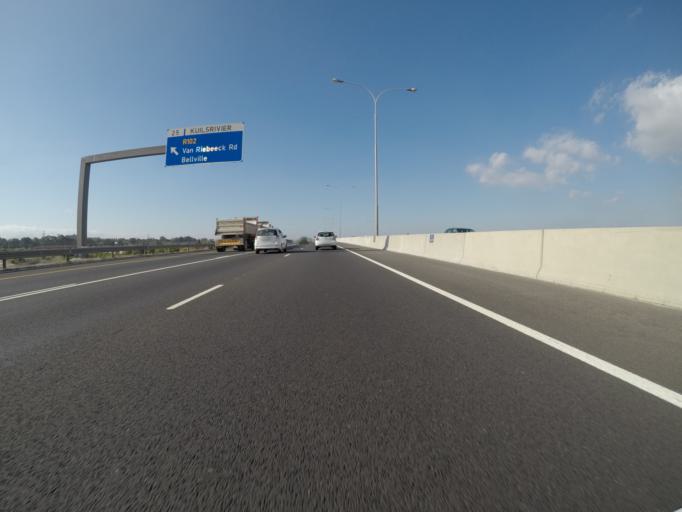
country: ZA
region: Western Cape
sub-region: City of Cape Town
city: Kraaifontein
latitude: -33.9197
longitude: 18.6653
